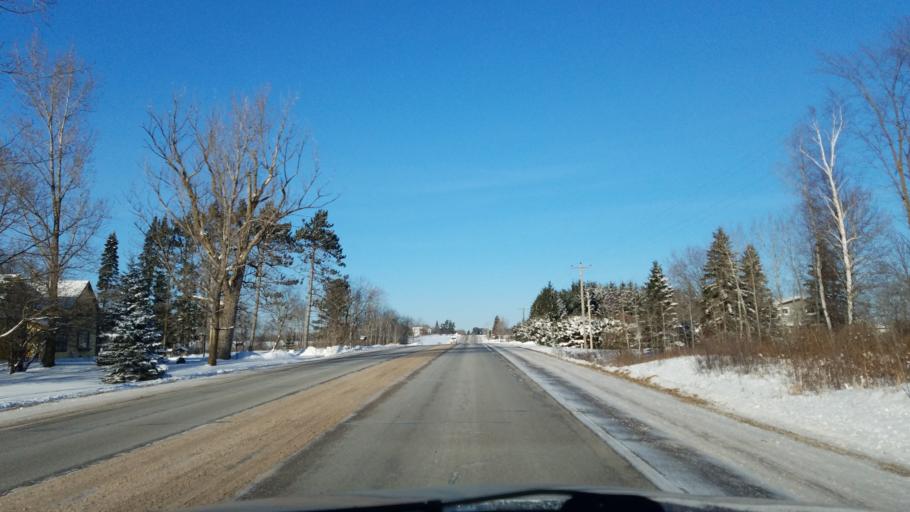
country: US
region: Wisconsin
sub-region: Barron County
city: Cumberland
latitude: 45.5115
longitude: -92.0522
